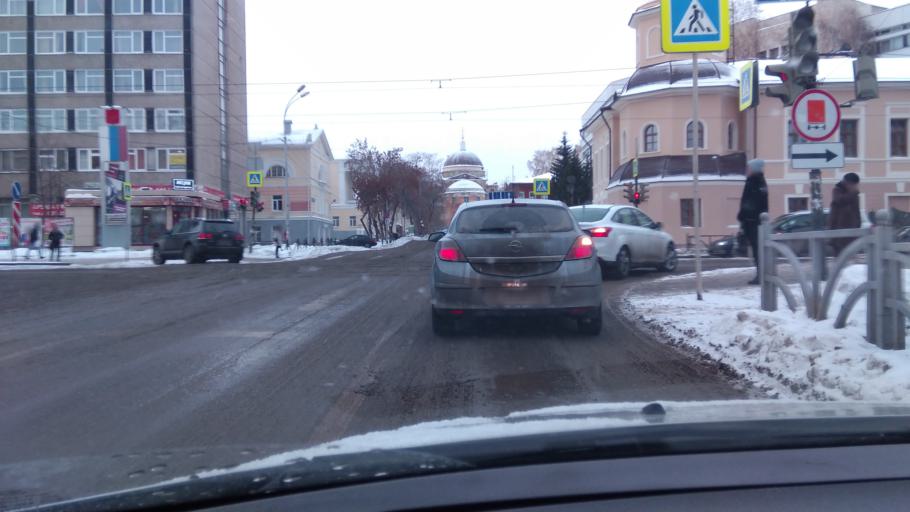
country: RU
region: Sverdlovsk
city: Yekaterinburg
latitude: 56.8227
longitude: 60.6051
